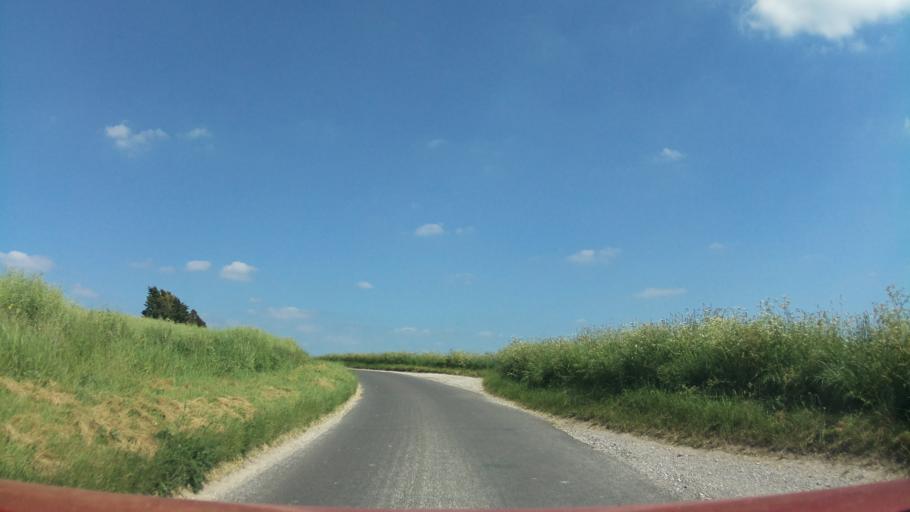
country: GB
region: England
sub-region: Wiltshire
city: Collingbourne Kingston
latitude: 51.2819
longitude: -1.6790
